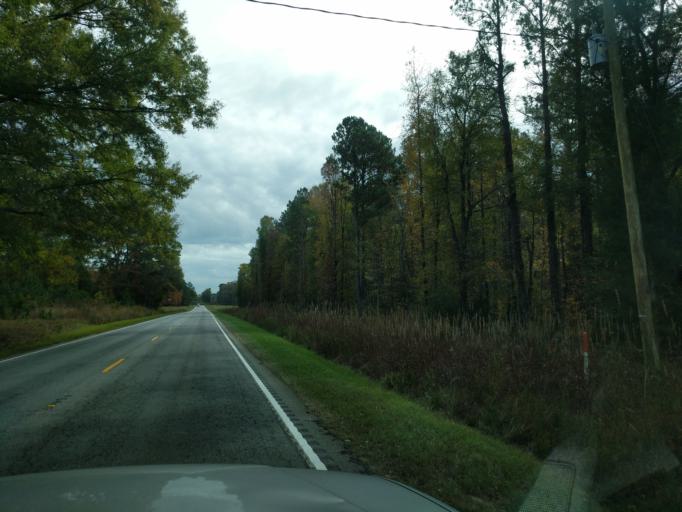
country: US
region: South Carolina
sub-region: Greenwood County
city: Ninety Six
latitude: 34.1981
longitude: -81.8846
